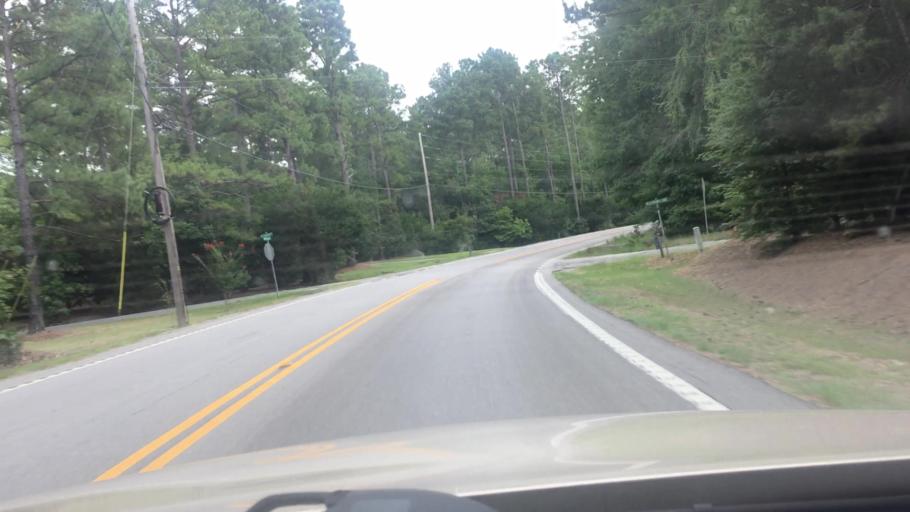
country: US
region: South Carolina
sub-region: Lexington County
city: Irmo
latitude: 34.1414
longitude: -81.1897
